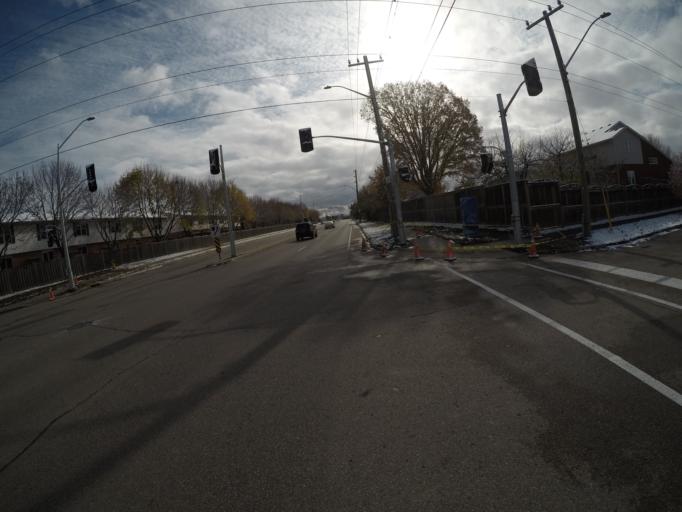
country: CA
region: Ontario
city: Waterloo
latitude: 43.5000
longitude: -80.4936
